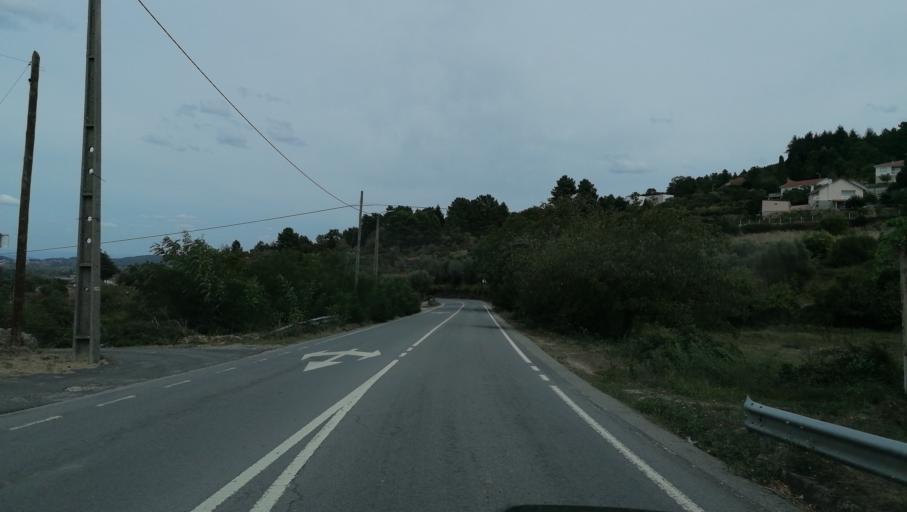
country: PT
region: Vila Real
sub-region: Vila Pouca de Aguiar
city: Vila Pouca de Aguiar
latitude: 41.5299
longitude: -7.6123
